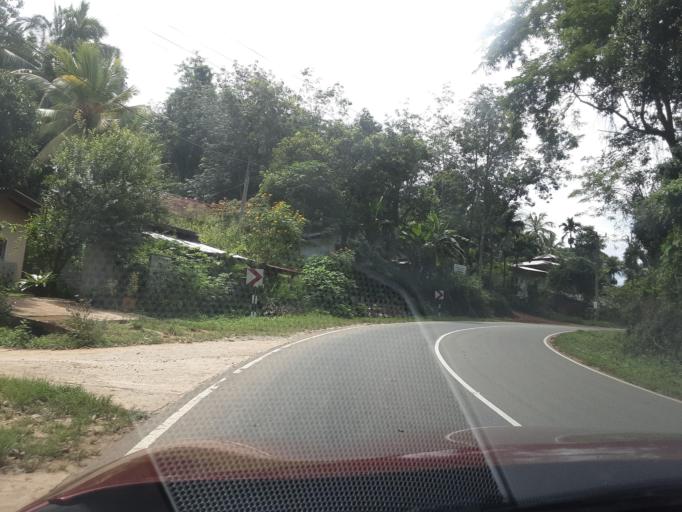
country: LK
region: Uva
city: Monaragala
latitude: 6.8958
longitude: 81.2466
